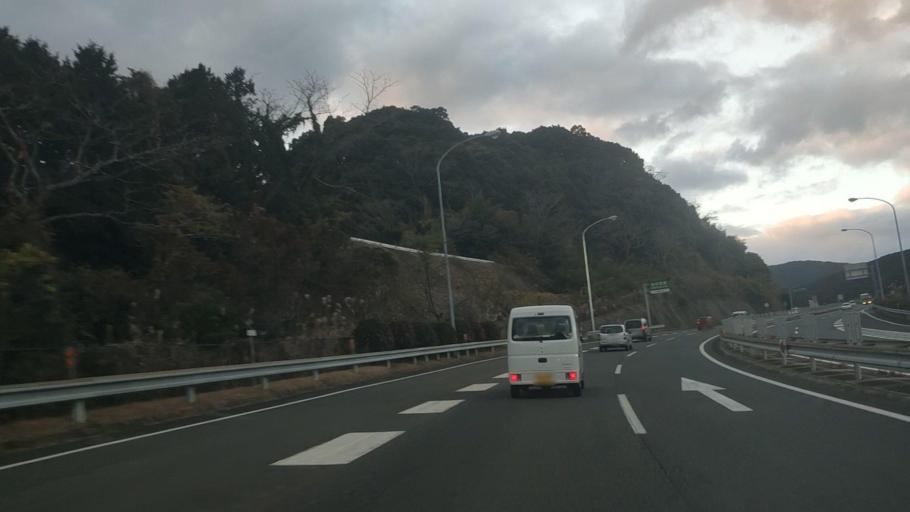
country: JP
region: Nagasaki
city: Obita
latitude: 32.8131
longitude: 129.9569
